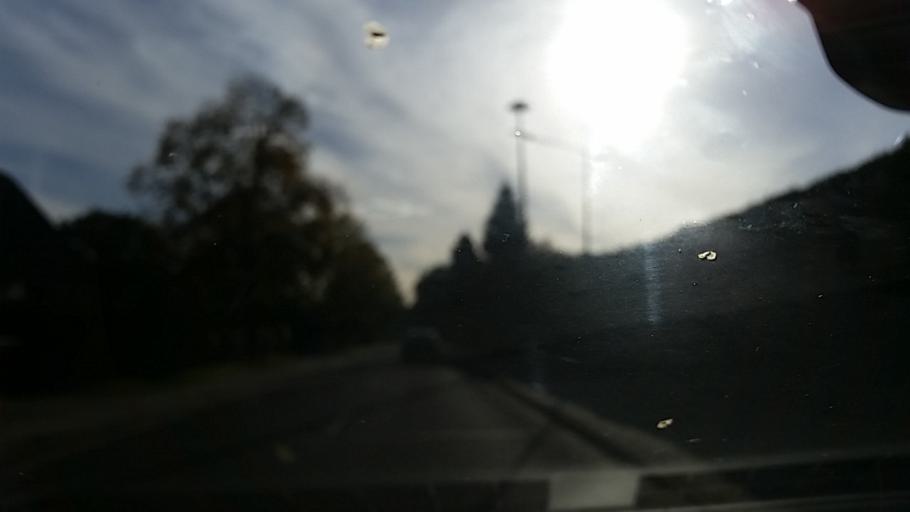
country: DE
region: Schleswig-Holstein
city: Kayhude
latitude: 53.7371
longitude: 10.1549
